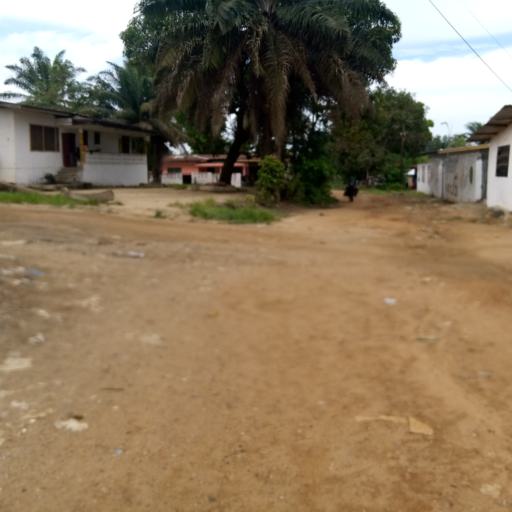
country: LR
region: Montserrado
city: Monrovia
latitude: 6.2959
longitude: -10.6993
